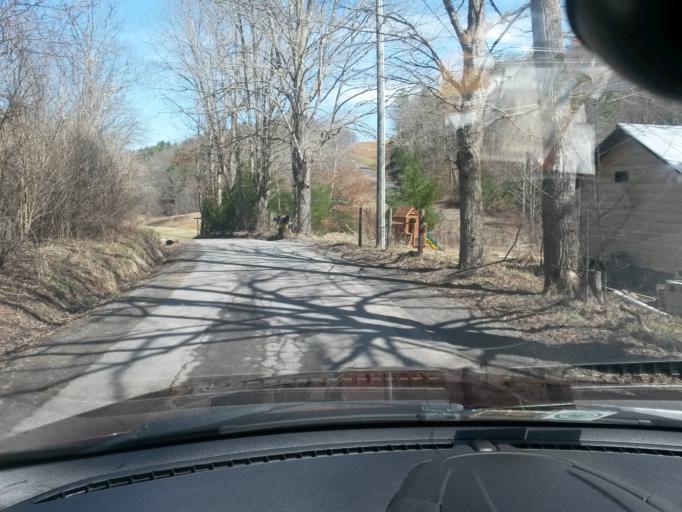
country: US
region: West Virginia
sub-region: Greenbrier County
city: White Sulphur Springs
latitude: 37.6422
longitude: -80.3333
